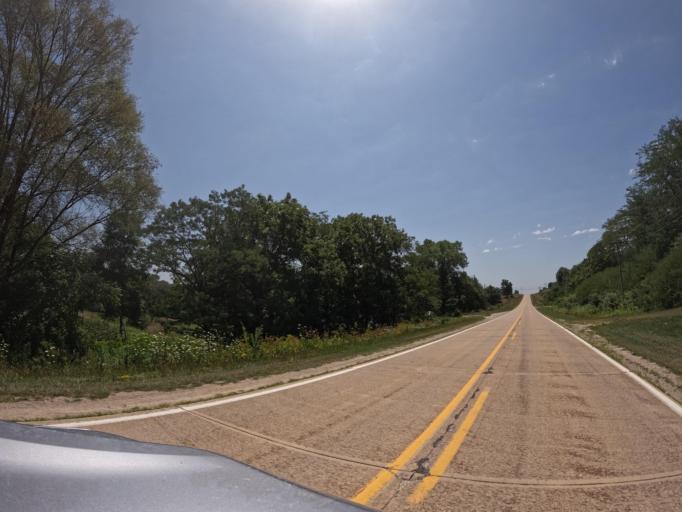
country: US
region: Iowa
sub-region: Henry County
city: Mount Pleasant
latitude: 40.9394
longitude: -91.5545
